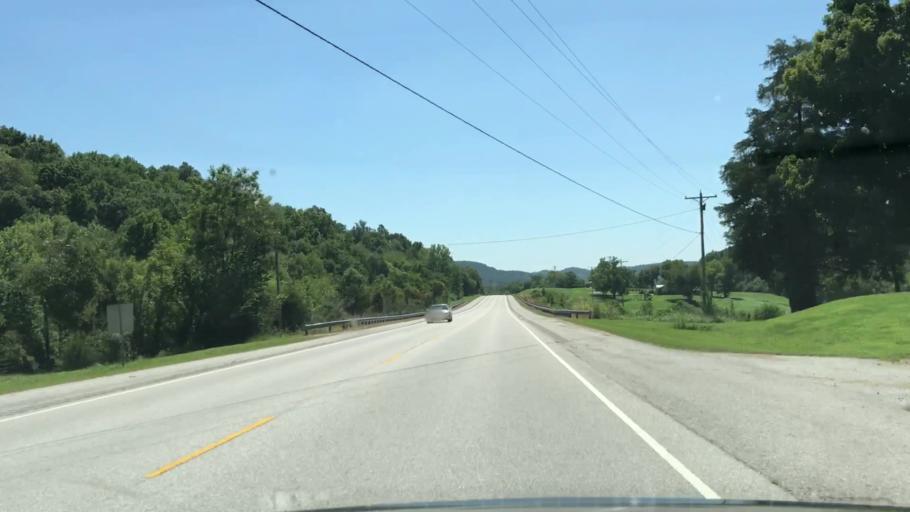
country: US
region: Tennessee
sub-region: Jackson County
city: Gainesboro
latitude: 36.4203
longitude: -85.6397
